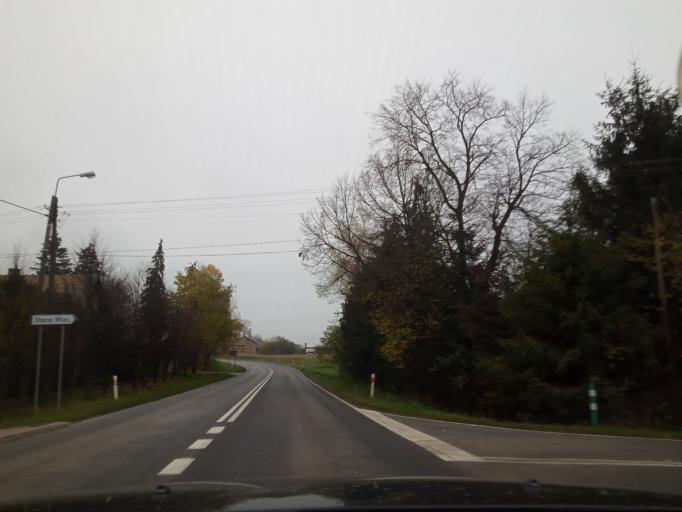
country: PL
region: Lesser Poland Voivodeship
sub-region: Powiat proszowicki
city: Klimontow
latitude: 50.2248
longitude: 20.3174
